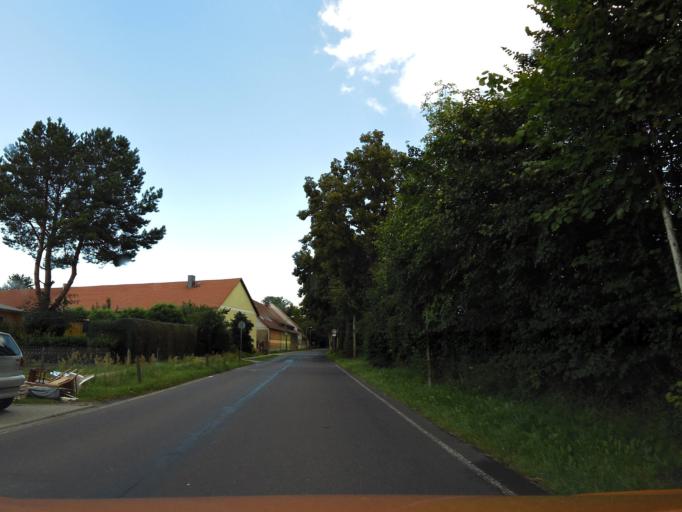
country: DE
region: Brandenburg
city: Potsdam
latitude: 52.4641
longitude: 13.0095
